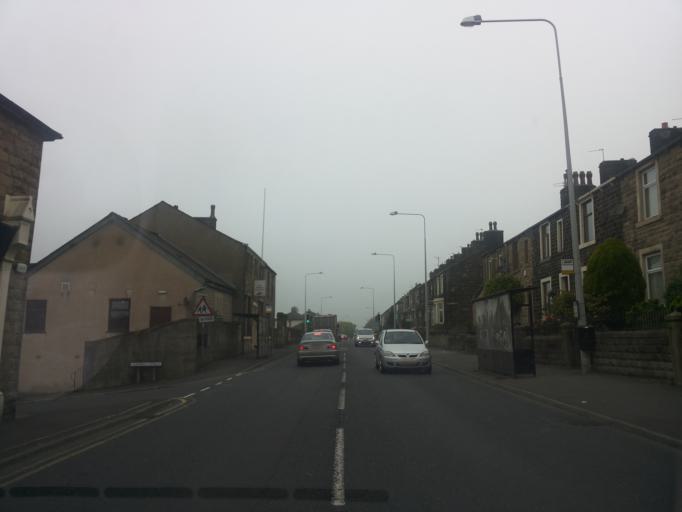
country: GB
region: England
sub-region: Lancashire
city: Padiham
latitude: 53.8064
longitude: -2.3536
